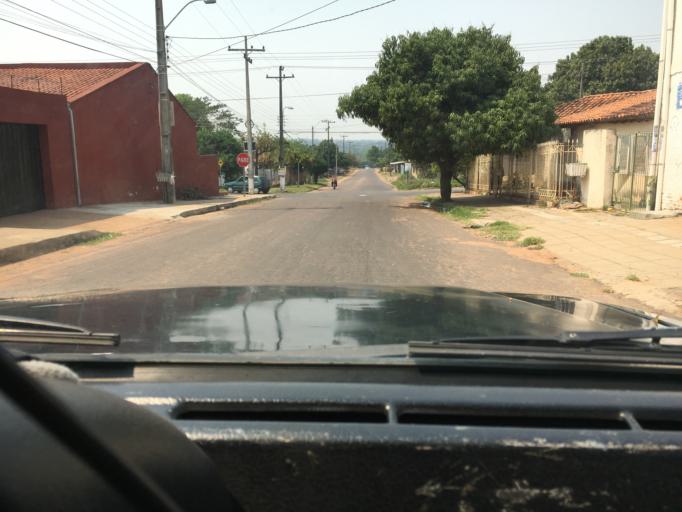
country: PY
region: Central
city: Villa Elisa
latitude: -25.3852
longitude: -57.5800
